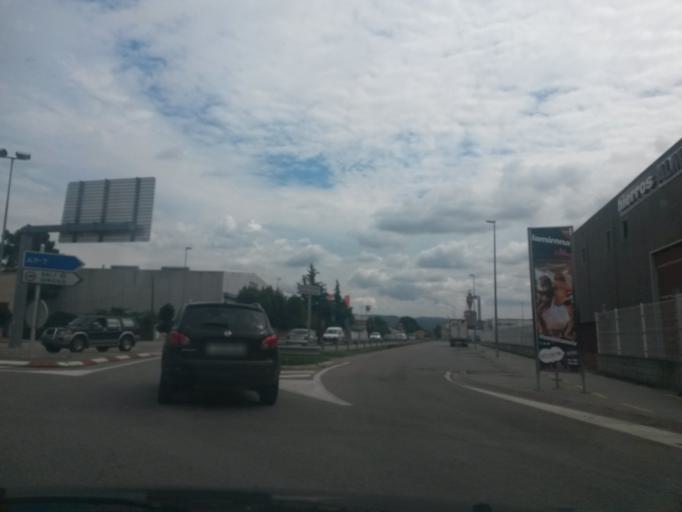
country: ES
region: Catalonia
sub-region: Provincia de Girona
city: Vilablareix
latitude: 41.9695
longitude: 2.7731
